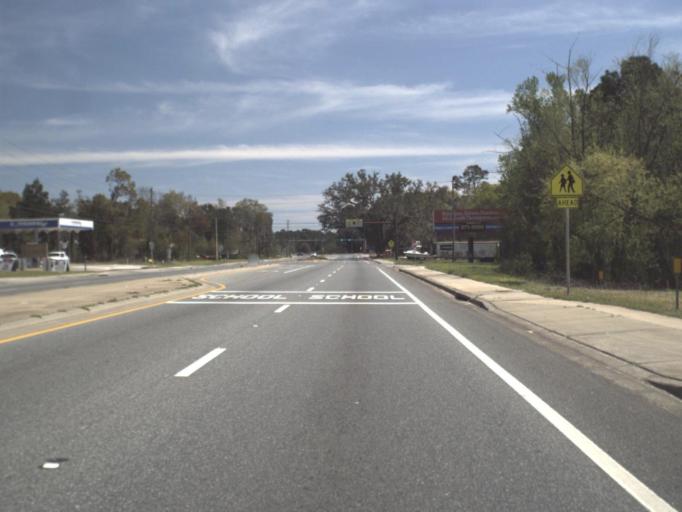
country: US
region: Florida
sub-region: Bay County
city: Lynn Haven
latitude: 30.2926
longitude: -85.6429
